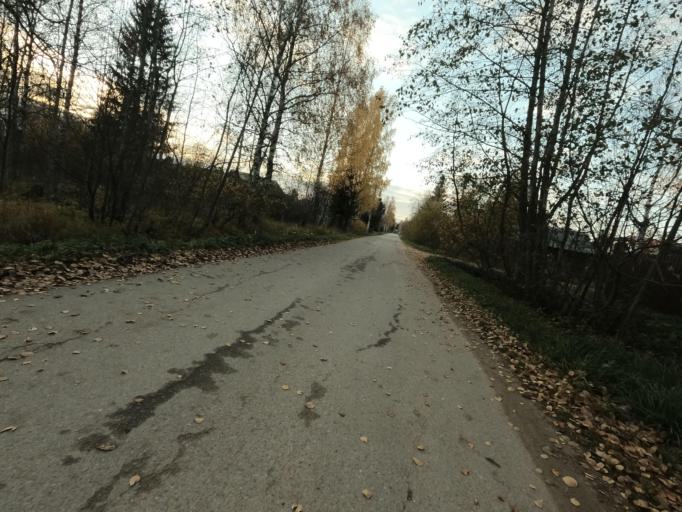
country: RU
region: Leningrad
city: Mga
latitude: 59.7757
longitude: 31.2117
